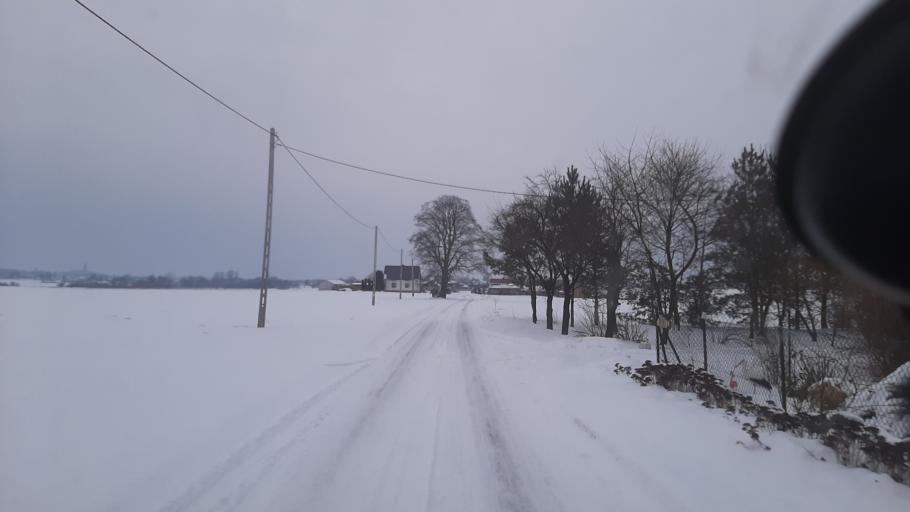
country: PL
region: Lublin Voivodeship
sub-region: Powiat lubelski
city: Garbow
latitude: 51.3557
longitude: 22.3883
